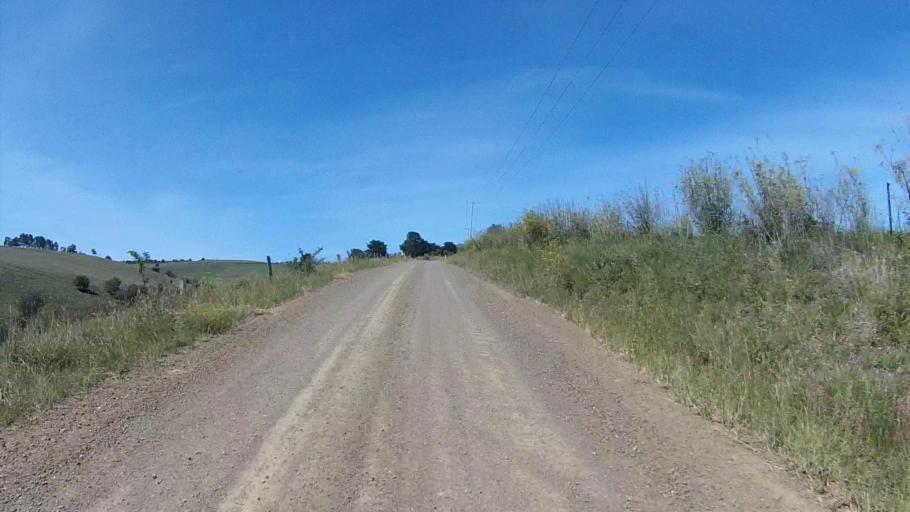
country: AU
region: Tasmania
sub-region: Sorell
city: Sorell
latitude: -42.7546
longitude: 147.6254
